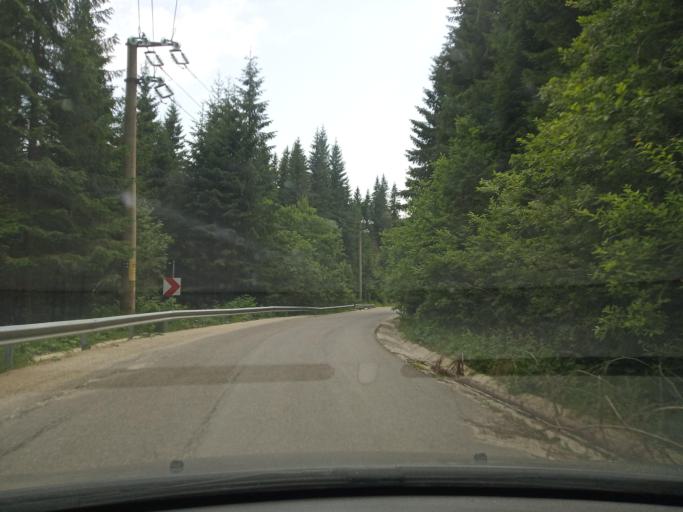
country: RO
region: Dambovita
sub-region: Comuna Moroeni
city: Glod
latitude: 45.3392
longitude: 25.4256
